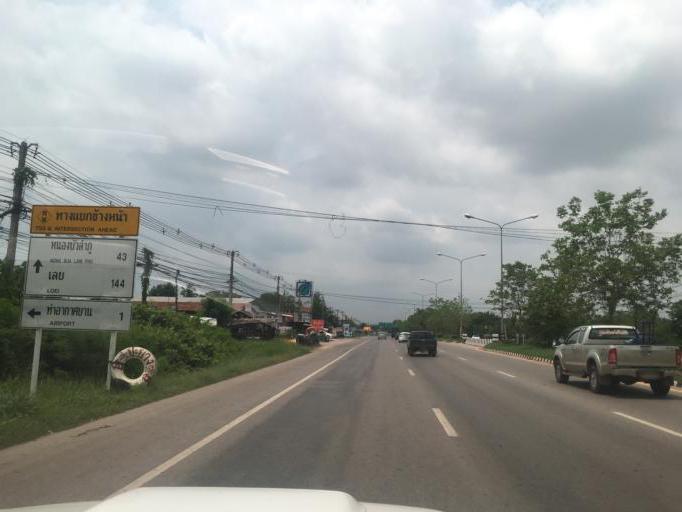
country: TH
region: Changwat Udon Thani
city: Udon Thani
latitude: 17.3948
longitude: 102.7661
